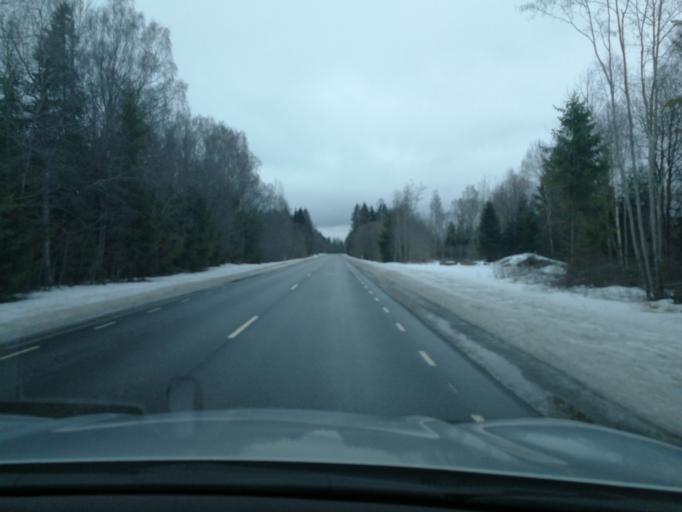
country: EE
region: Harju
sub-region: Anija vald
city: Kehra
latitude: 59.2668
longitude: 25.3543
